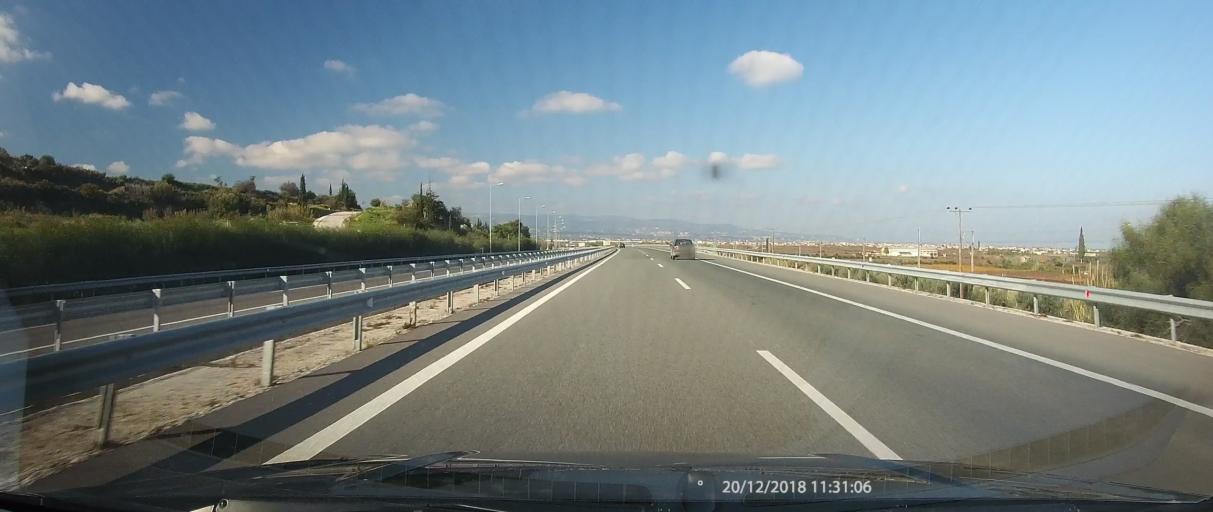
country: GR
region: Peloponnese
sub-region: Nomos Korinthias
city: Assos
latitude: 37.9189
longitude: 22.8221
